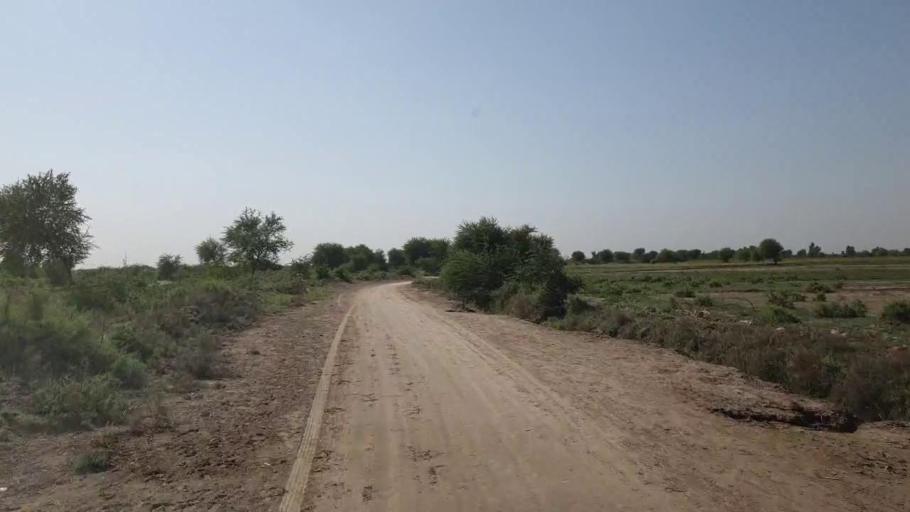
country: PK
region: Sindh
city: Tando Bago
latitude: 24.7361
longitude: 69.0212
